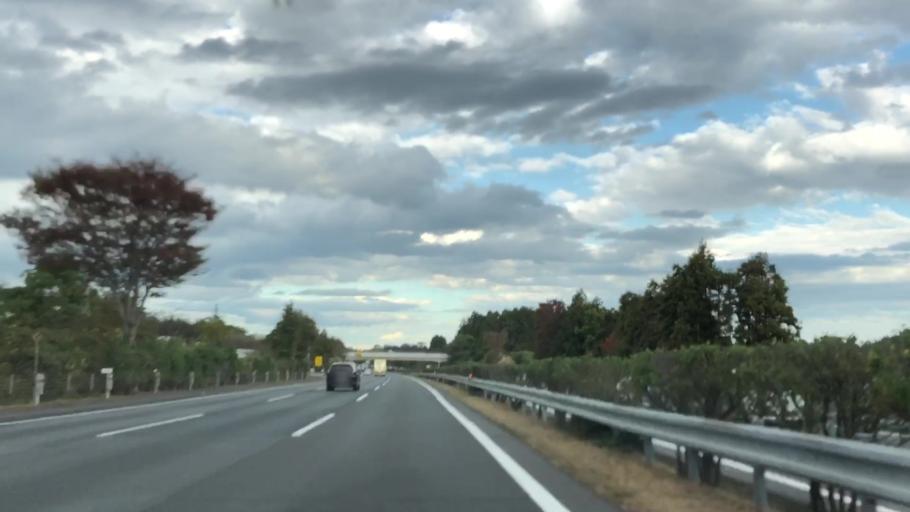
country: JP
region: Ibaraki
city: Ishioka
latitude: 36.1386
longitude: 140.2037
